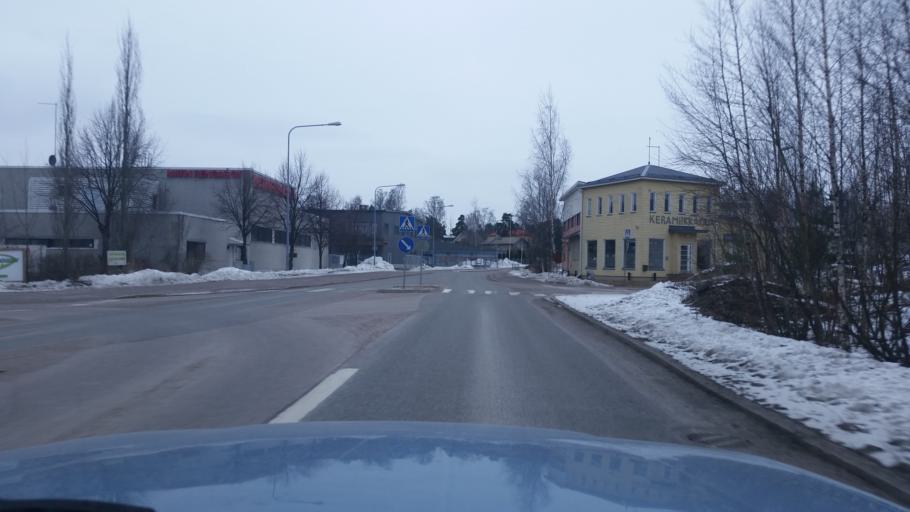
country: FI
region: Uusimaa
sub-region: Helsinki
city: Vantaa
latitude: 60.2581
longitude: 25.0208
